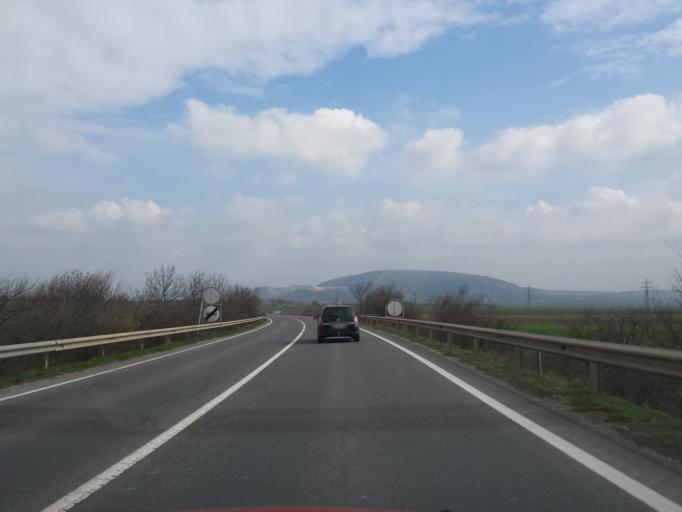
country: AT
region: Lower Austria
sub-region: Politischer Bezirk Bruck an der Leitha
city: Petronell-Carnuntum
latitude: 48.1060
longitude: 16.8708
